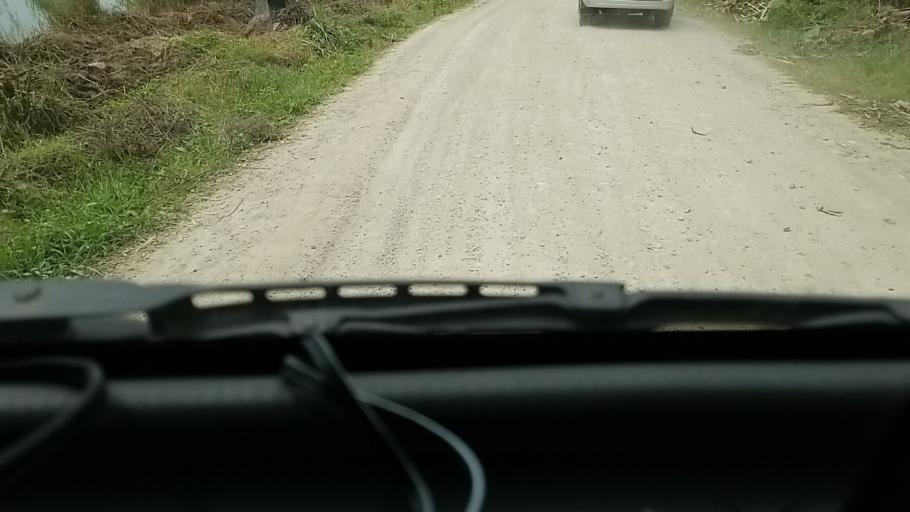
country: CD
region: Nord Kivu
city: Sake
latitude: -1.6007
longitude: 29.0374
